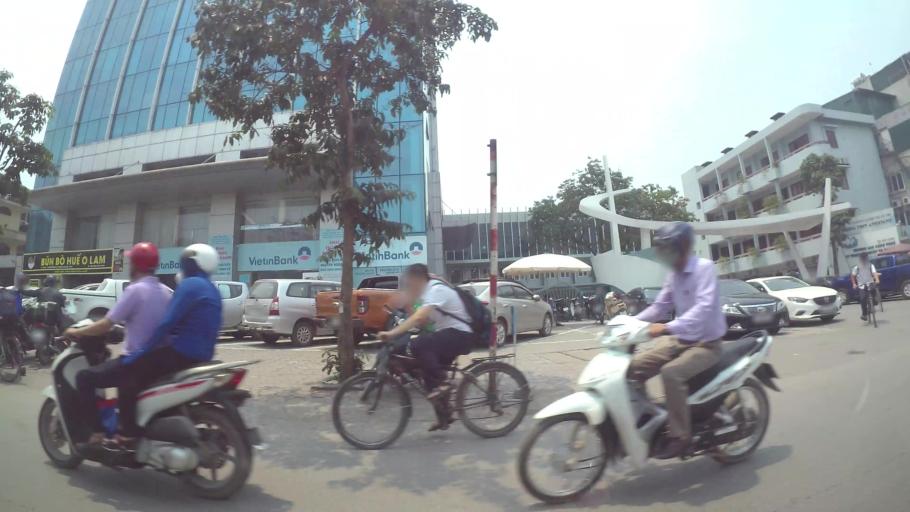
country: VN
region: Ha Noi
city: Thanh Xuan
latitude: 21.0121
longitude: 105.8074
